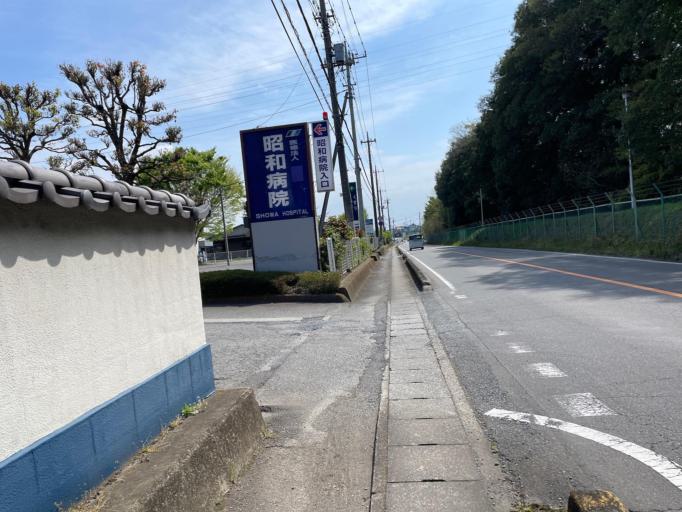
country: JP
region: Gunma
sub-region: Sawa-gun
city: Tamamura
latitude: 36.3037
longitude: 139.0812
